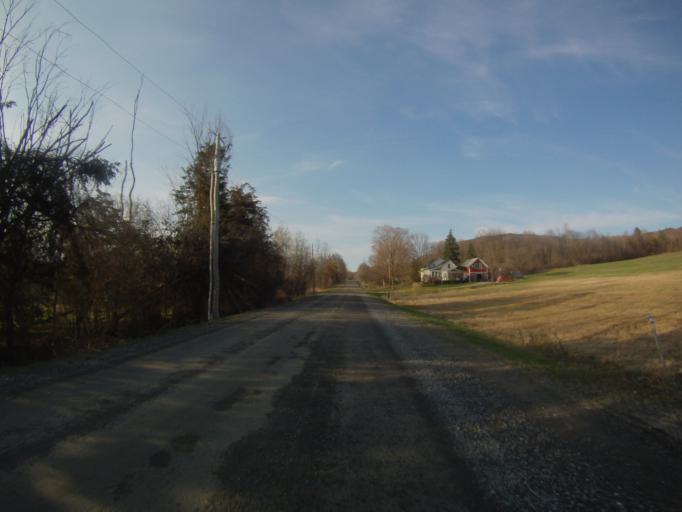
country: US
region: Vermont
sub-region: Addison County
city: Middlebury (village)
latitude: 44.0419
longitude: -73.2929
